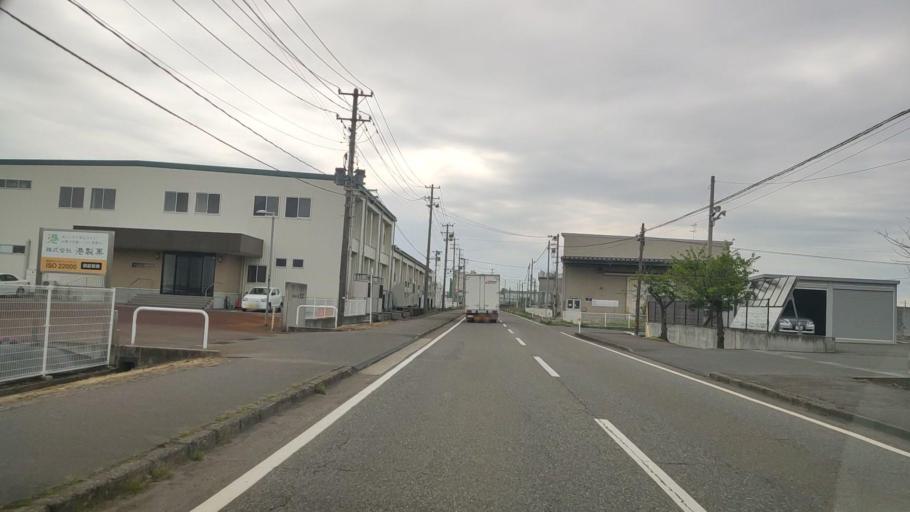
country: JP
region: Niigata
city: Niigata-shi
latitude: 37.9483
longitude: 139.0796
